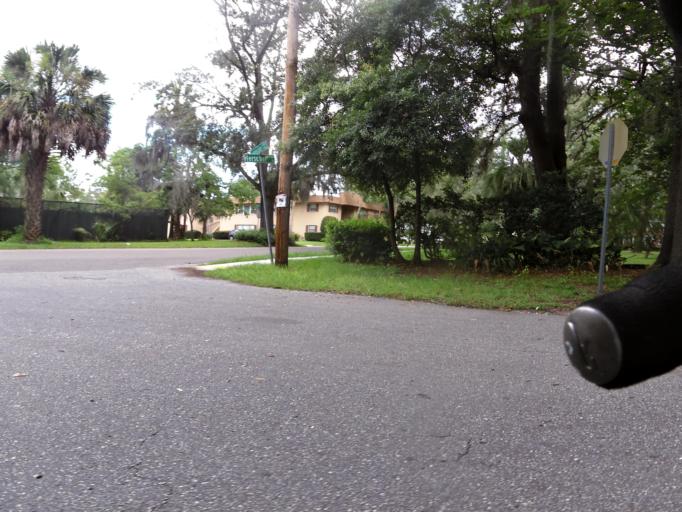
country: US
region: Florida
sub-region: Duval County
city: Jacksonville
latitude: 30.2802
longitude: -81.7134
